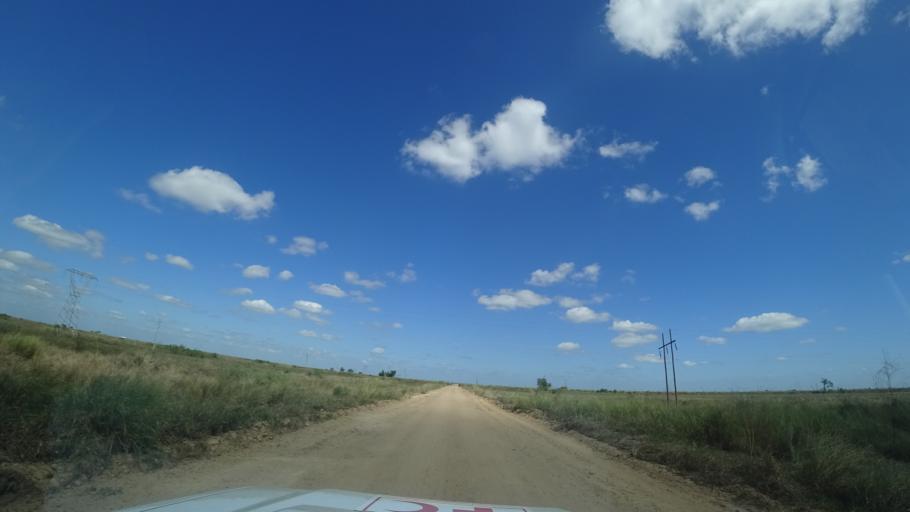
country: MZ
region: Sofala
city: Dondo
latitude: -19.4634
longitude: 34.5618
